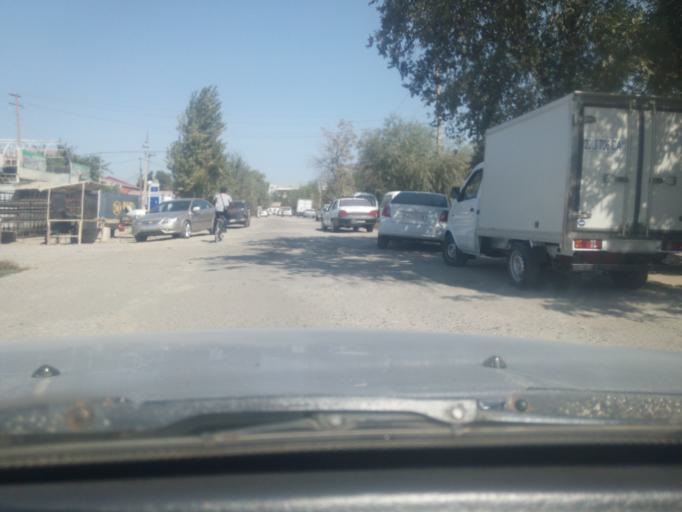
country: UZ
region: Sirdaryo
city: Guliston
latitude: 40.4913
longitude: 68.7730
